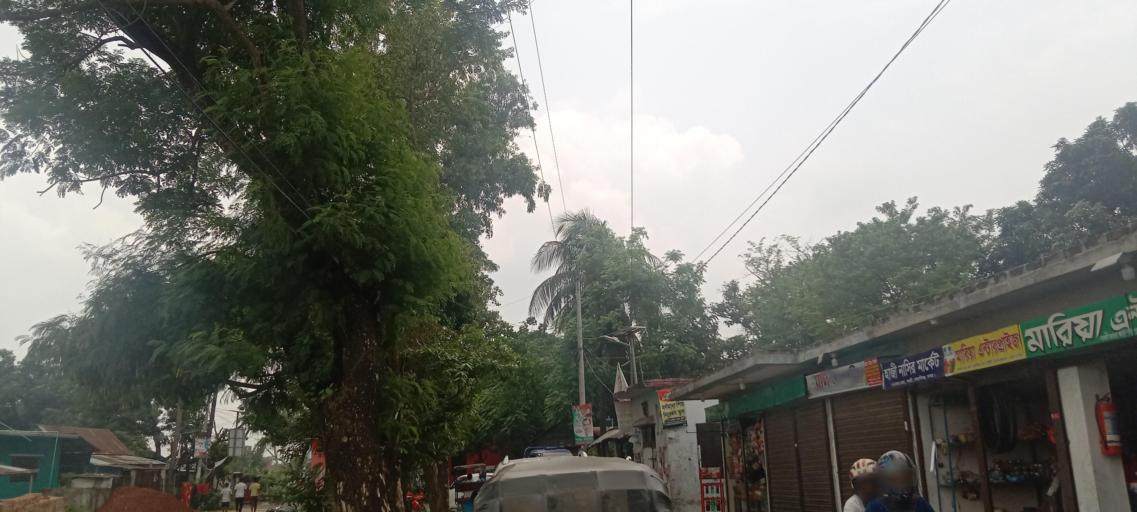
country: BD
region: Dhaka
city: Azimpur
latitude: 23.7117
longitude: 90.3457
